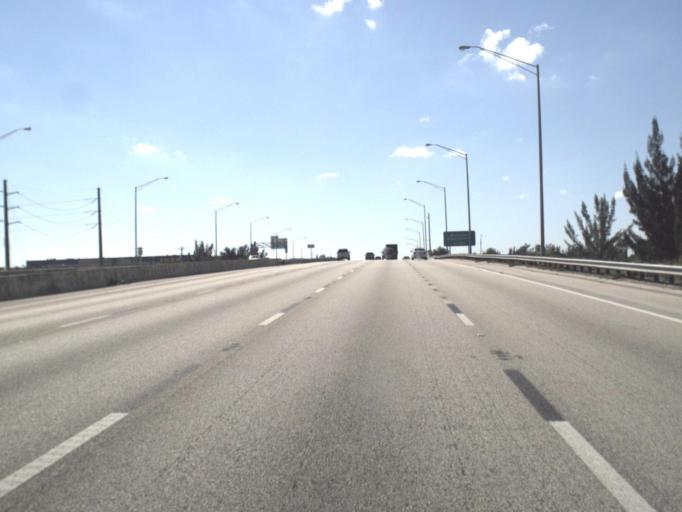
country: US
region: Florida
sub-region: Miami-Dade County
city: Doral
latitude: 25.7991
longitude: -80.3862
